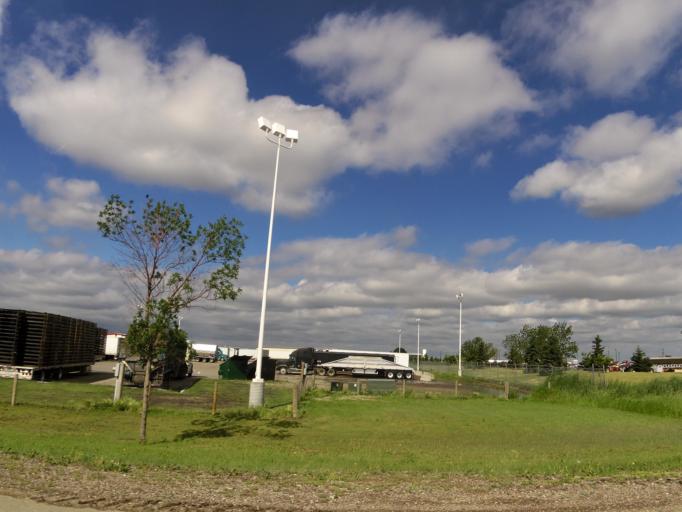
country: US
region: North Dakota
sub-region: Grand Forks County
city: Grand Forks
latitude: 47.9349
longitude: -97.0953
